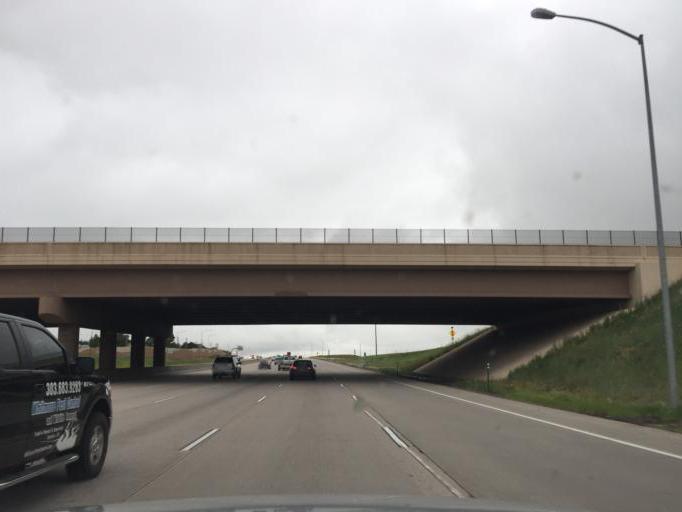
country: US
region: Colorado
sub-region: Park County
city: Castle Pines North
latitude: 39.4714
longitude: -104.8725
